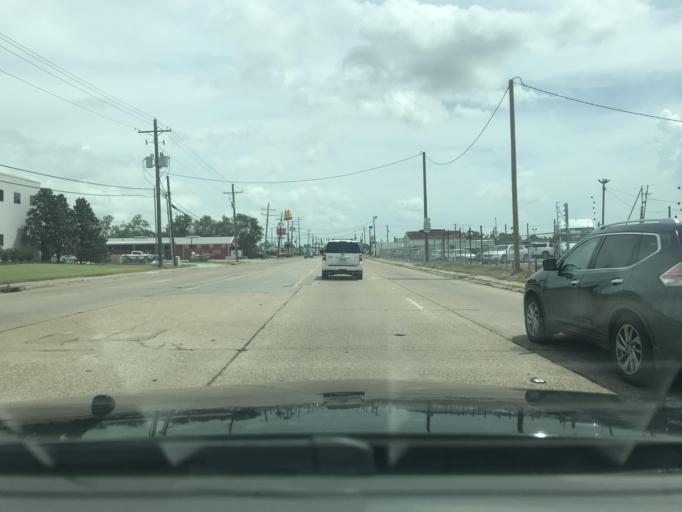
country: US
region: Louisiana
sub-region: Calcasieu Parish
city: Lake Charles
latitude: 30.2297
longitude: -93.1802
